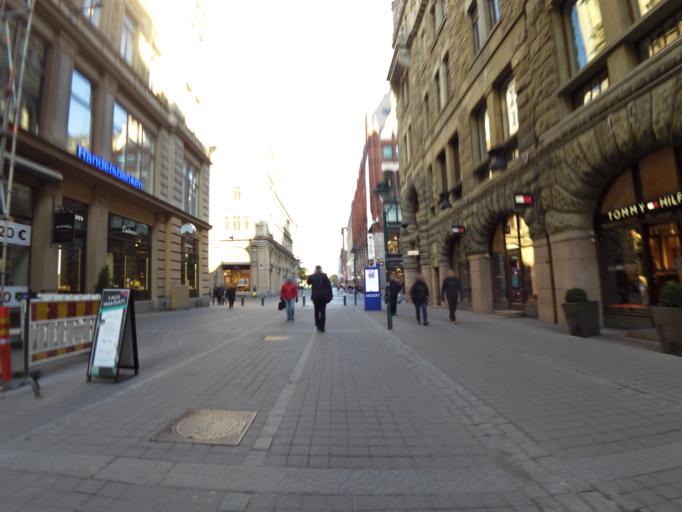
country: FI
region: Uusimaa
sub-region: Helsinki
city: Helsinki
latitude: 60.1685
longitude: 24.9456
